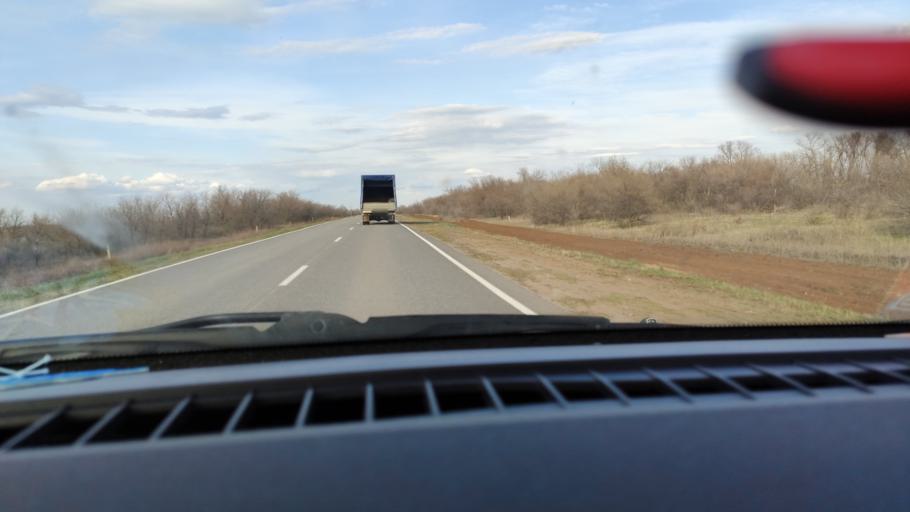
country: RU
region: Saratov
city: Privolzhskiy
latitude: 51.2884
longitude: 45.9759
